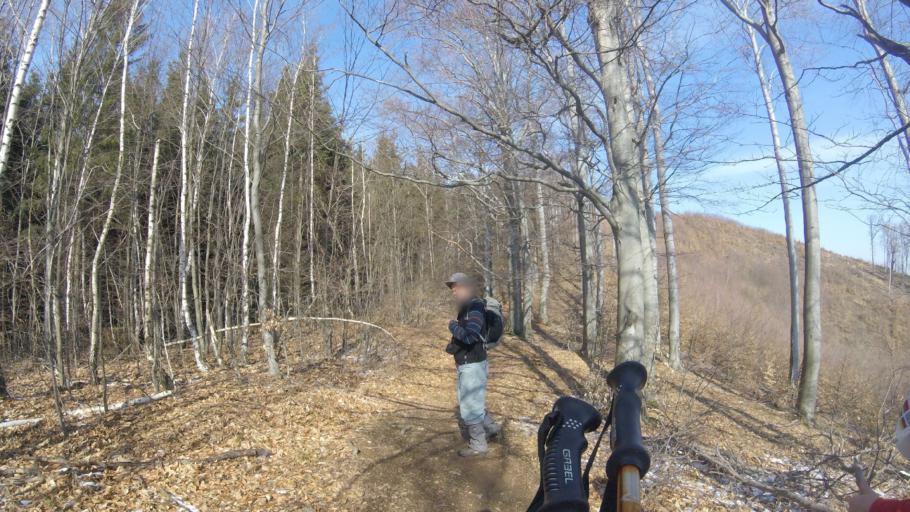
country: HU
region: Heves
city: Paradsasvar
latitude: 47.9095
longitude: 19.9469
